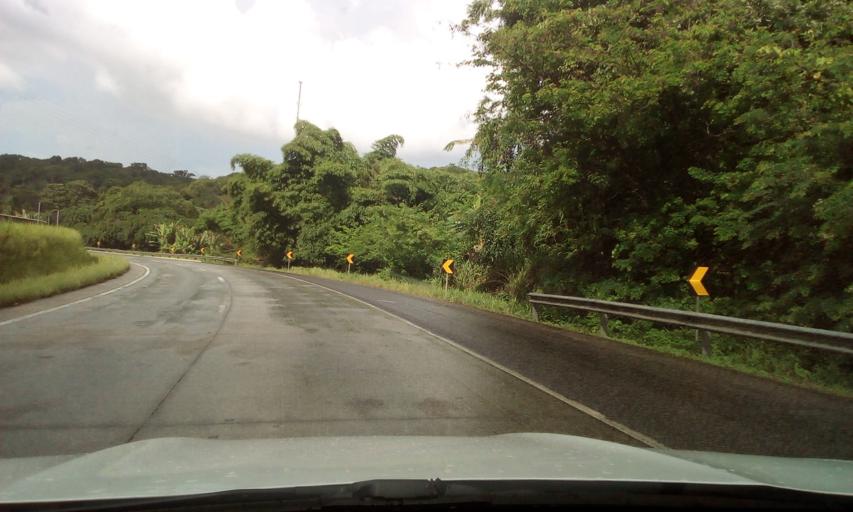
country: BR
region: Pernambuco
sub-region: Cabo De Santo Agostinho
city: Cabo
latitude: -8.3056
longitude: -35.0963
